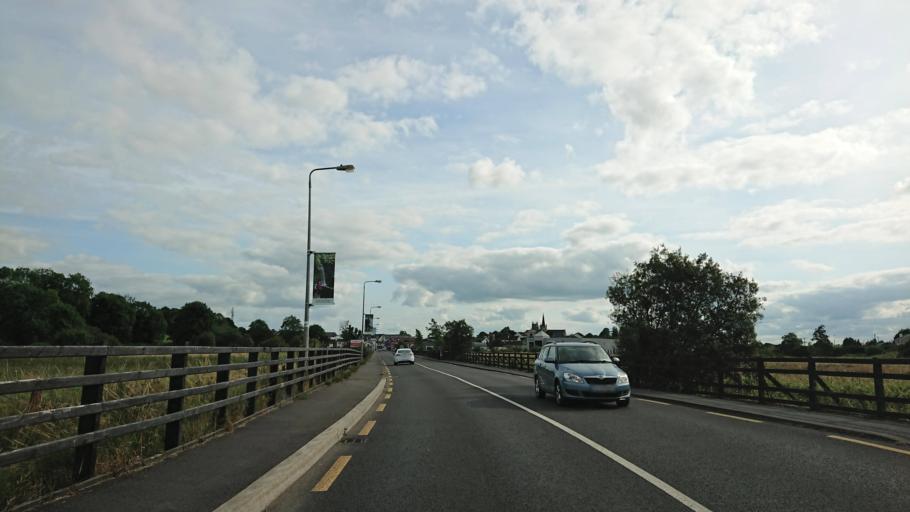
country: IE
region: Connaught
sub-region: County Leitrim
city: Carrick-on-Shannon
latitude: 53.9523
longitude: -8.0904
